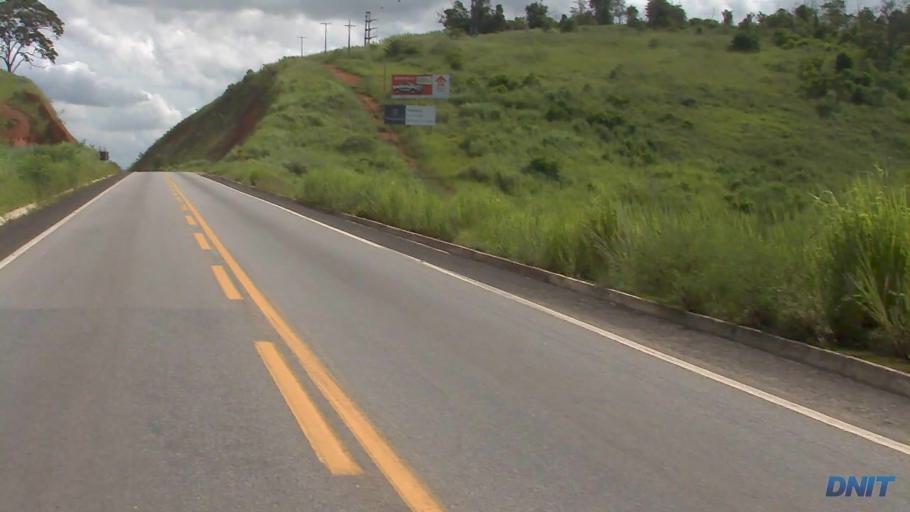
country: BR
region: Minas Gerais
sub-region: Ipatinga
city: Ipatinga
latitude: -19.4164
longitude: -42.4924
